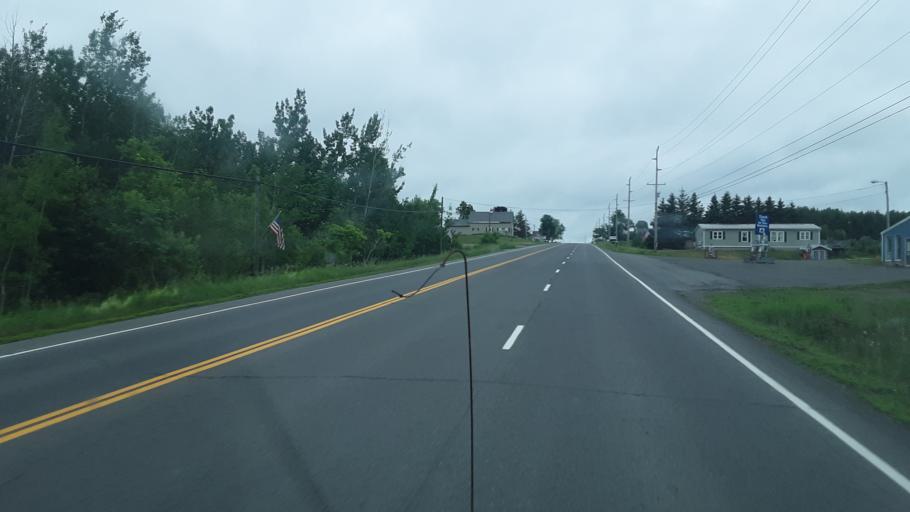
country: US
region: Maine
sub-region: Penobscot County
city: Patten
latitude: 45.9873
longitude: -68.4496
